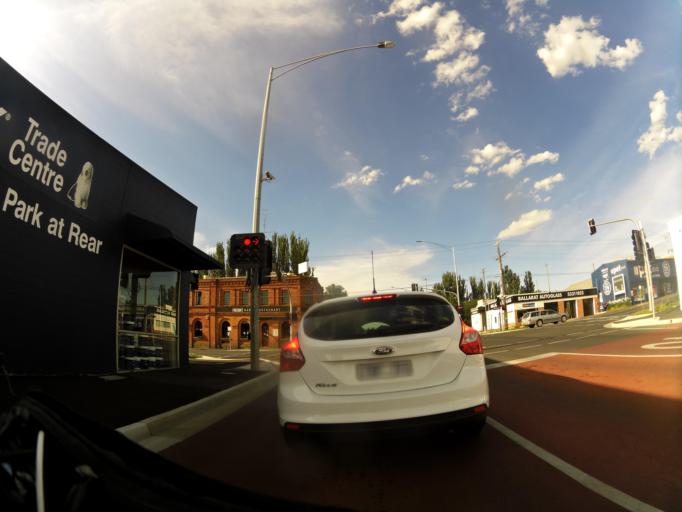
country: AU
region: Victoria
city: Ballarat East
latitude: -37.5606
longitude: 143.8641
